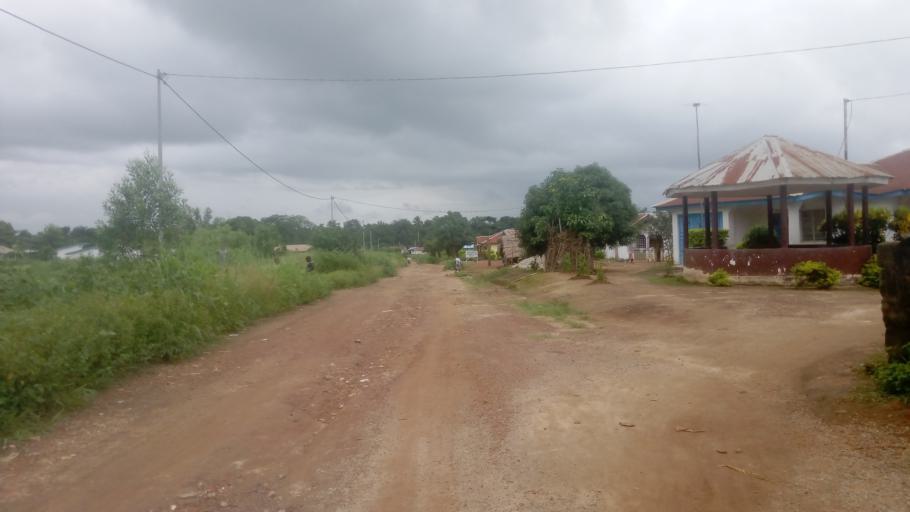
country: SL
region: Northern Province
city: Lunsar
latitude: 8.6845
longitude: -12.5489
